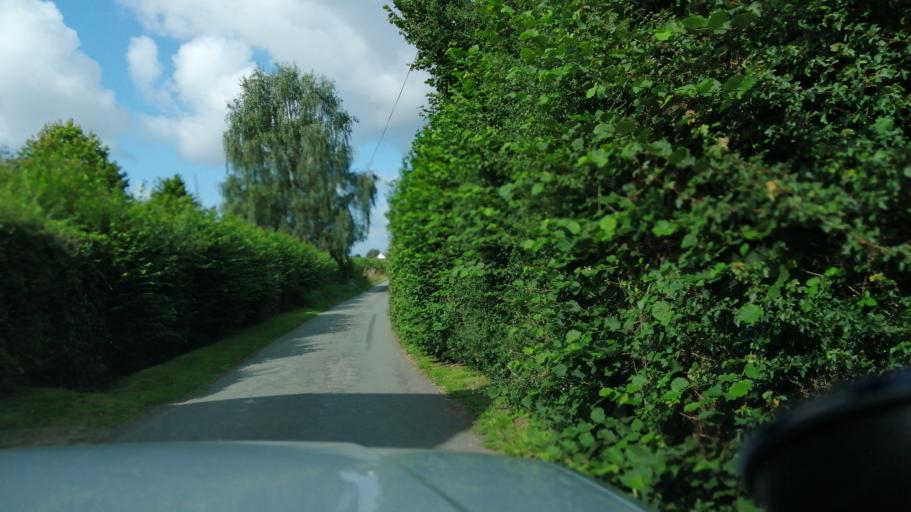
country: GB
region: England
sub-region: Herefordshire
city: Thruxton
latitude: 52.0199
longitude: -2.7925
